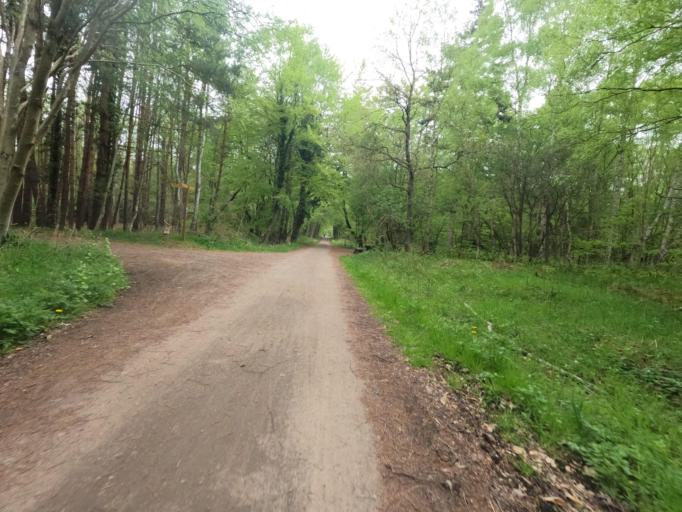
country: DE
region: Mecklenburg-Vorpommern
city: Born
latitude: 54.4250
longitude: 12.5008
